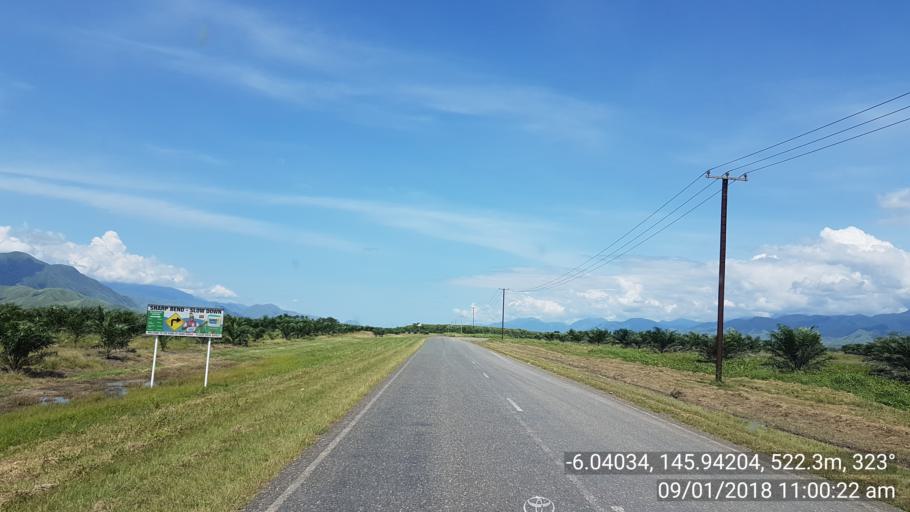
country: PG
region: Eastern Highlands
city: Kainantu
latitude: -6.0399
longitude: 145.9422
